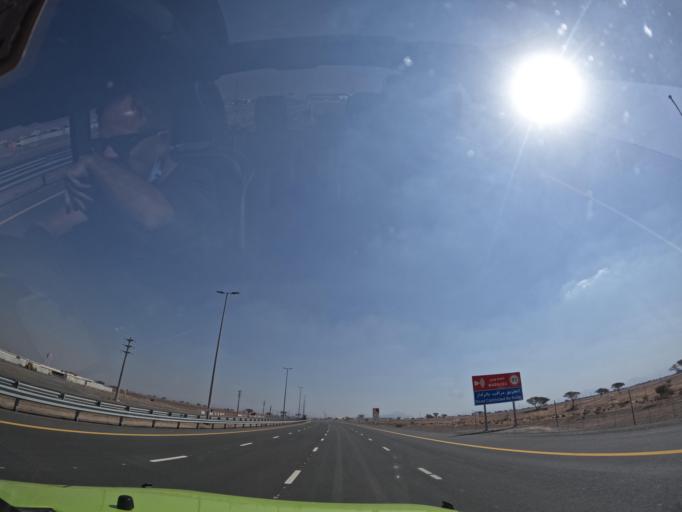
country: AE
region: Ash Shariqah
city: Adh Dhayd
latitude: 24.9111
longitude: 55.7840
